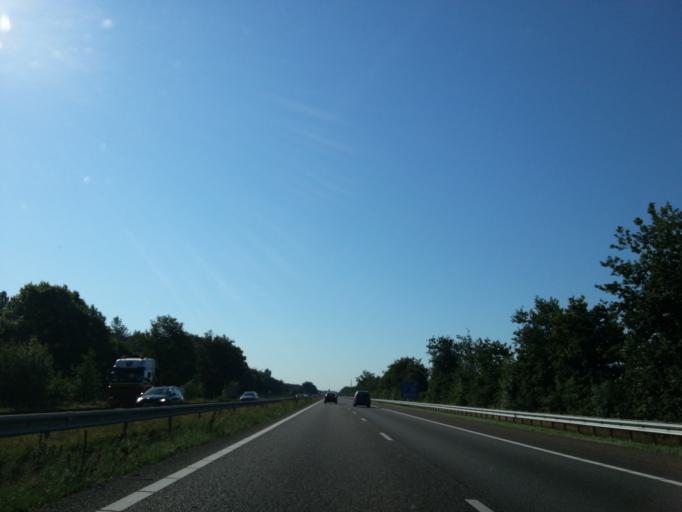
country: NL
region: North Brabant
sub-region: Gemeente Cranendonck
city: Cranendonck
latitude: 51.3305
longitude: 5.5844
